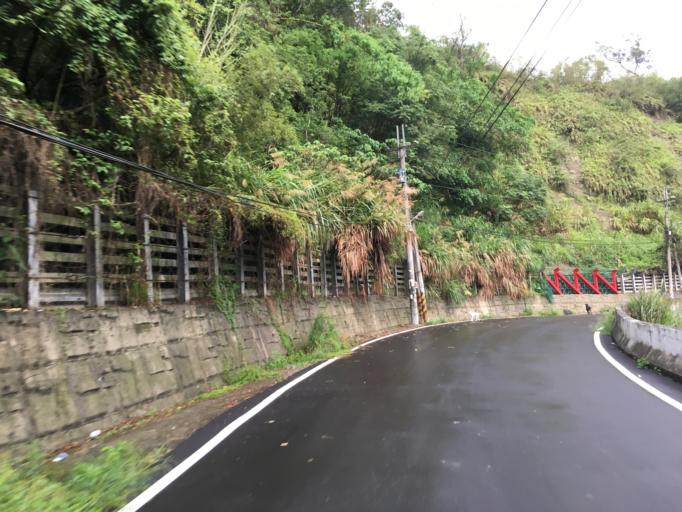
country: TW
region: Taiwan
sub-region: Taichung City
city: Taichung
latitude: 24.0604
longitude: 120.7415
